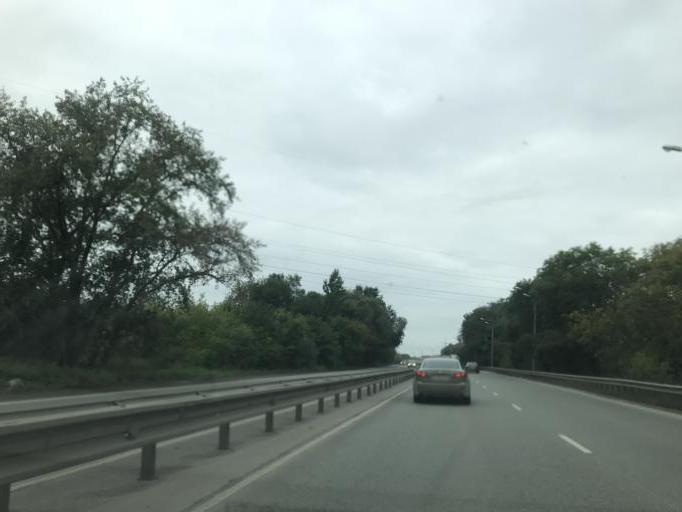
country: RU
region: Chelyabinsk
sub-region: Gorod Chelyabinsk
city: Chelyabinsk
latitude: 55.1707
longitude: 61.4276
